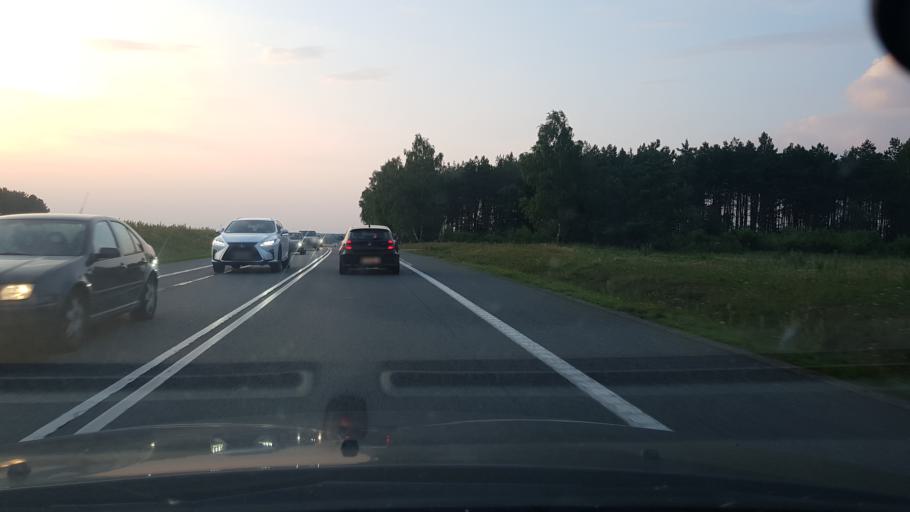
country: PL
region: Masovian Voivodeship
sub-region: Powiat mlawski
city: Wieczfnia Koscielna
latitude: 53.2081
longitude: 20.4329
